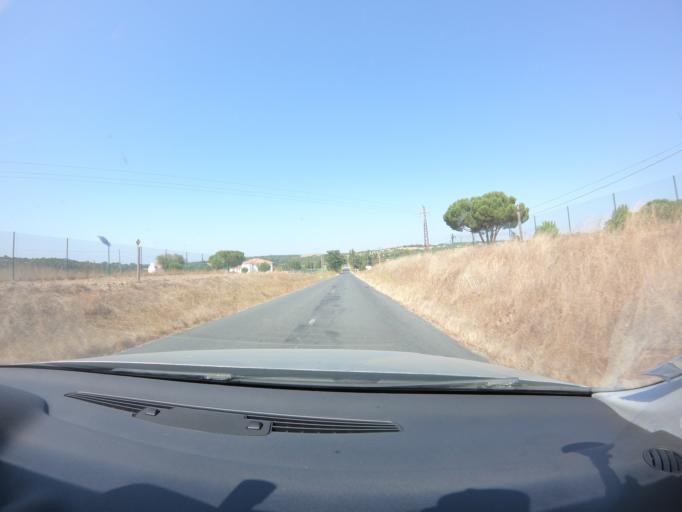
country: PT
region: Setubal
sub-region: Alcacer do Sal
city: Alcacer do Sal
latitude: 38.2828
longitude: -8.3993
